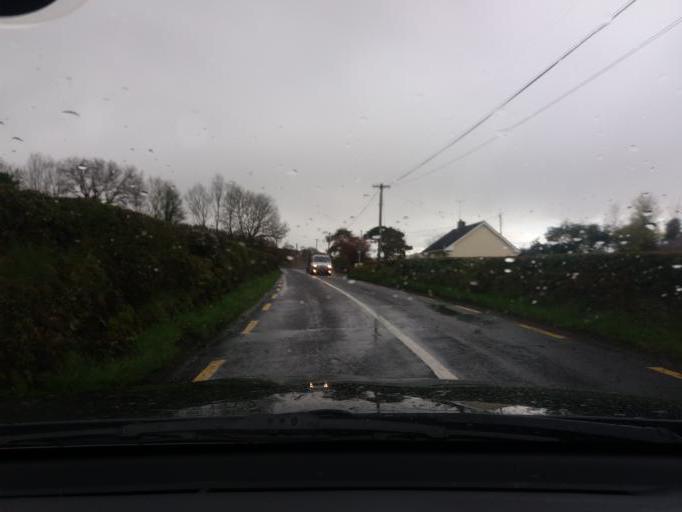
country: IE
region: Connaught
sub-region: County Leitrim
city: Manorhamilton
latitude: 54.2658
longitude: -7.9422
